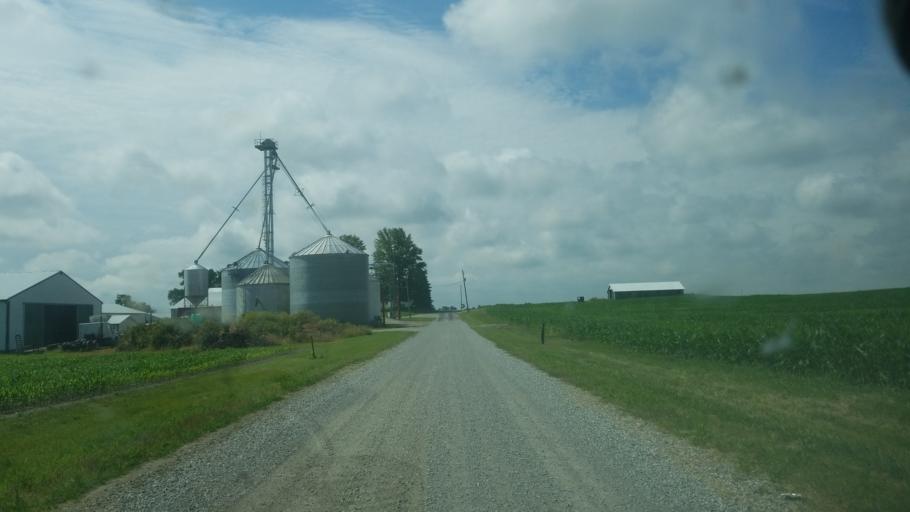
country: US
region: Ohio
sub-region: Licking County
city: Johnstown
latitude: 40.2097
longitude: -82.7398
